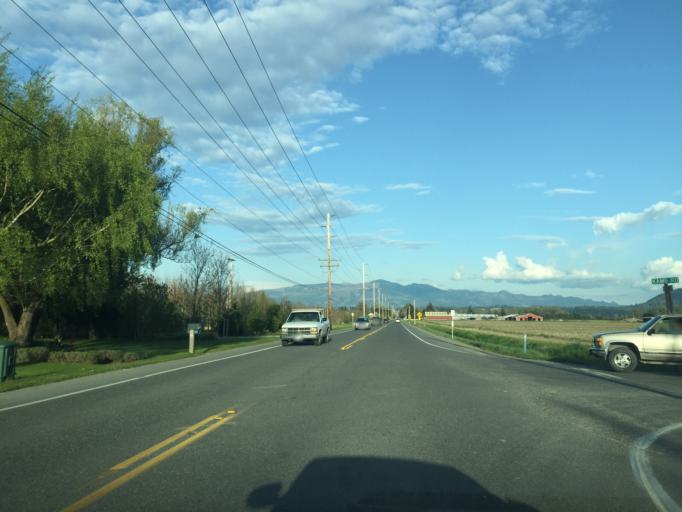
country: US
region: Washington
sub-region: Skagit County
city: Mount Vernon
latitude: 48.4209
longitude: -122.3845
